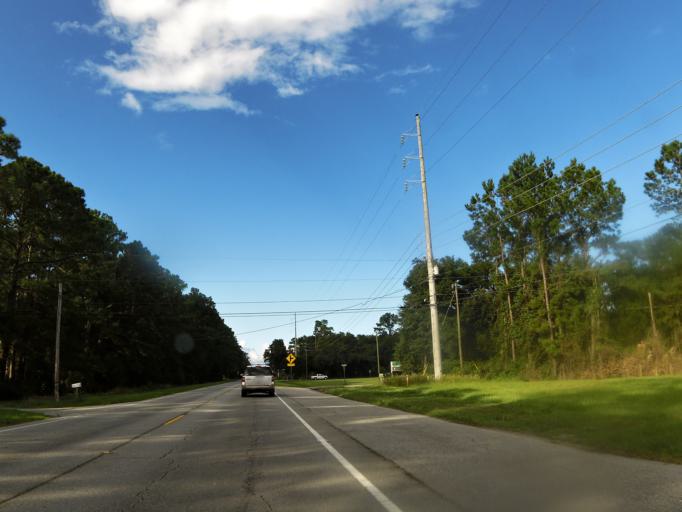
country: US
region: Georgia
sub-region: Glynn County
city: Country Club Estates
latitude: 31.2569
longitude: -81.4416
